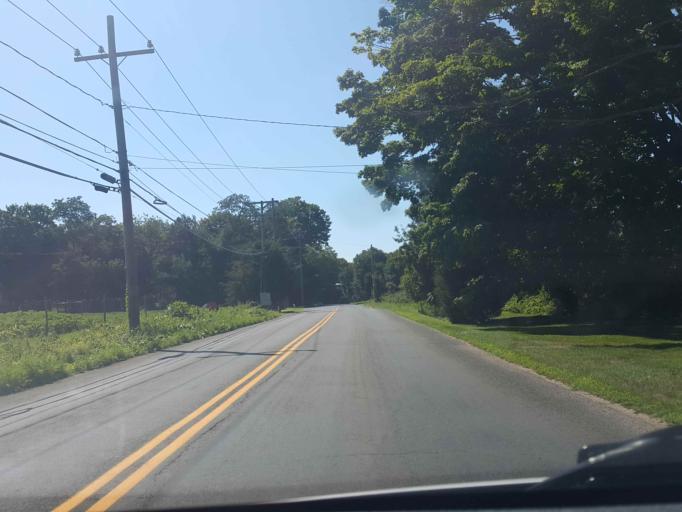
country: US
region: Connecticut
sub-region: New Haven County
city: Guilford
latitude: 41.2987
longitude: -72.6968
